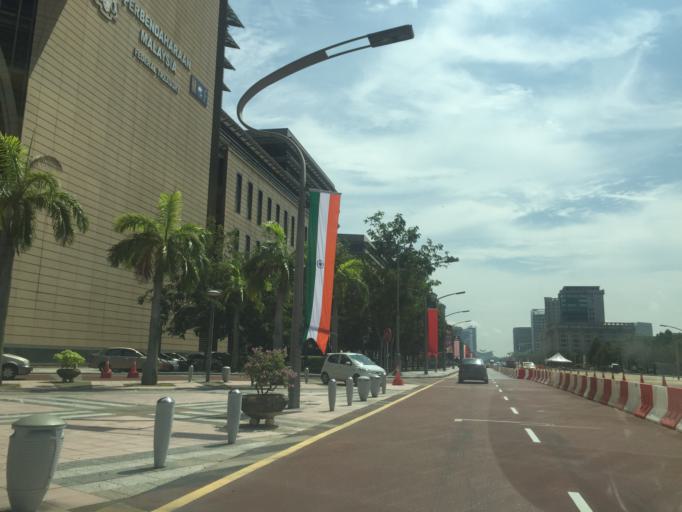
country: MY
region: Putrajaya
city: Putrajaya
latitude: 2.9262
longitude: 101.6882
